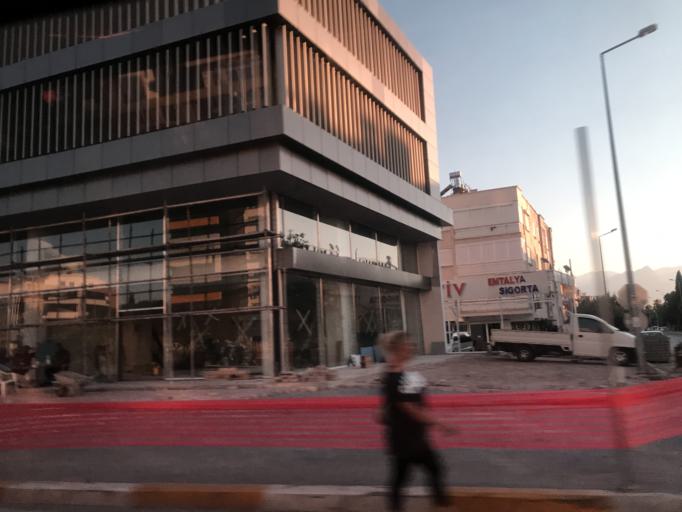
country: TR
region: Antalya
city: Antalya
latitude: 36.9084
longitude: 30.6804
